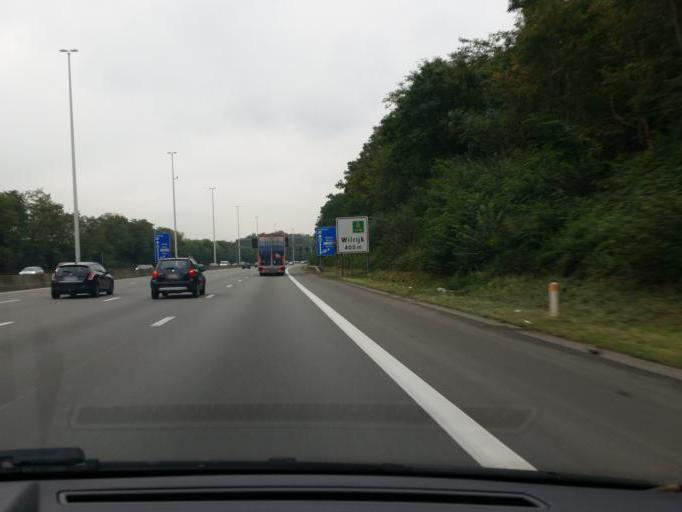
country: BE
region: Flanders
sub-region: Provincie Antwerpen
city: Edegem
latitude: 51.1606
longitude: 4.4160
